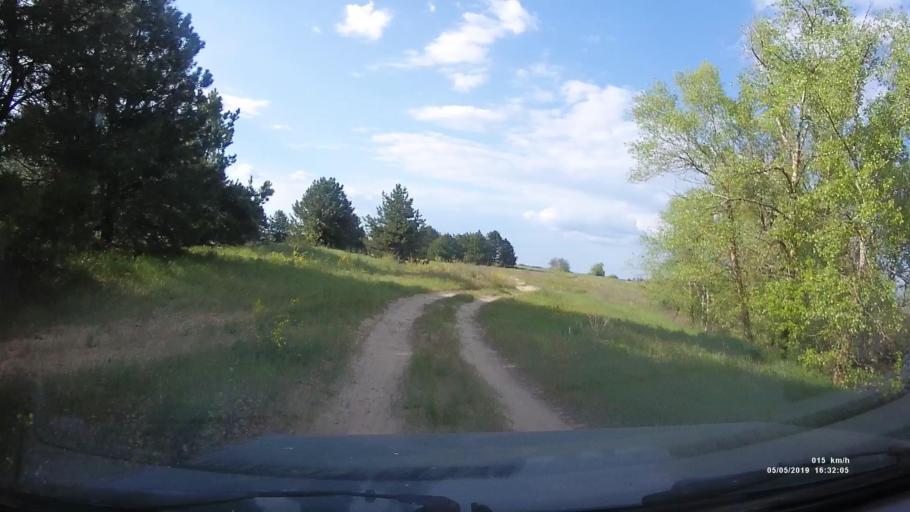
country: RU
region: Rostov
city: Ust'-Donetskiy
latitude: 47.7779
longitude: 41.0141
